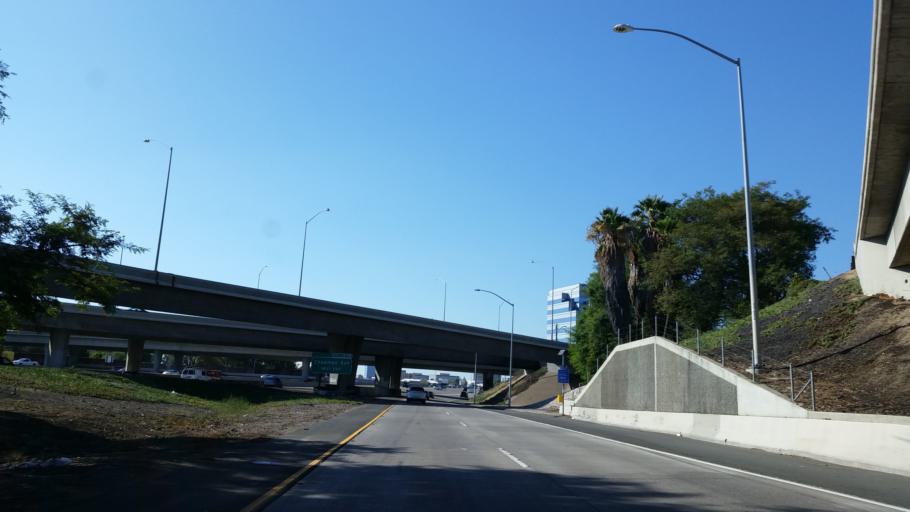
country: US
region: California
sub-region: Orange County
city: Orange
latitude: 33.7820
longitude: -117.8786
